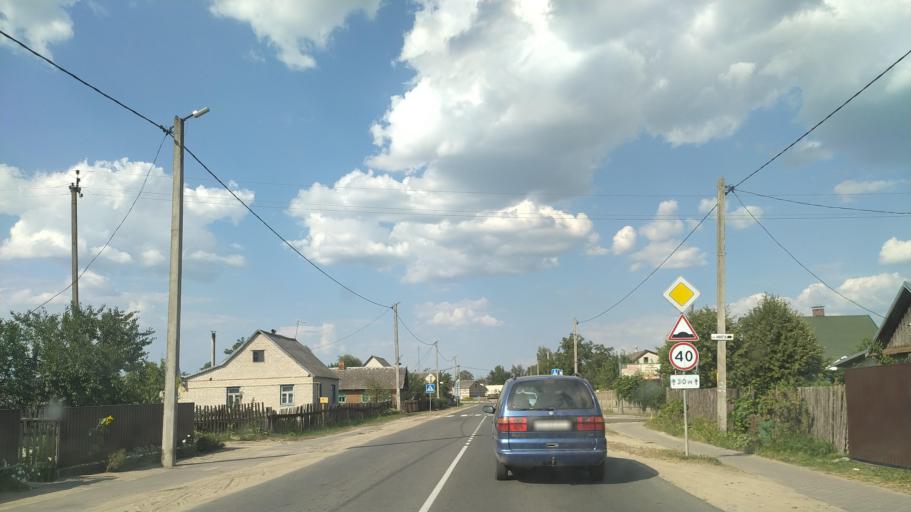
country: BY
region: Brest
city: Drahichyn
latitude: 52.1979
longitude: 25.1480
